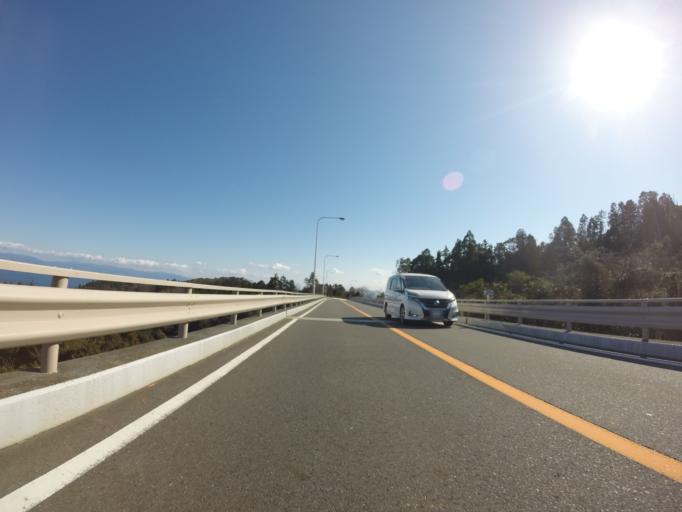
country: JP
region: Shizuoka
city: Shizuoka-shi
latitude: 34.9751
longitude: 138.4751
